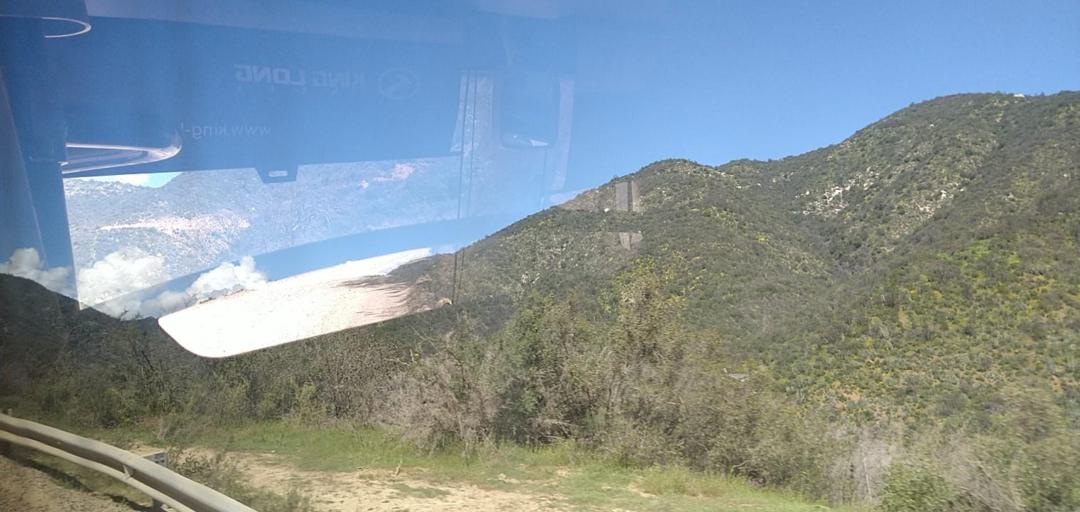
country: CL
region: Valparaiso
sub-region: Provincia de Marga Marga
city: Limache
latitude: -33.1986
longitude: -71.2680
